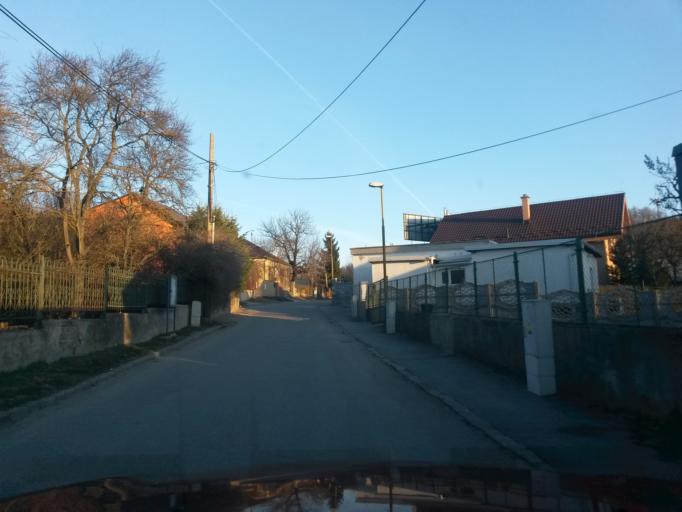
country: SK
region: Kosicky
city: Kosice
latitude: 48.7272
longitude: 21.2791
